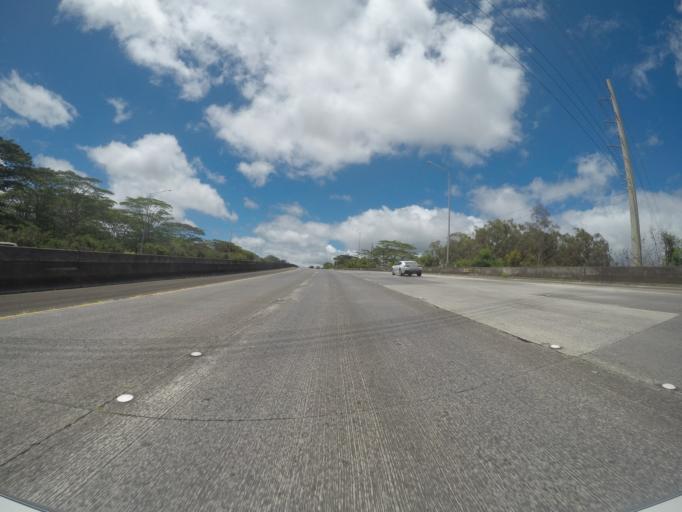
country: US
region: Hawaii
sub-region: Honolulu County
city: Mililani Town
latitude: 21.4468
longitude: -157.9911
